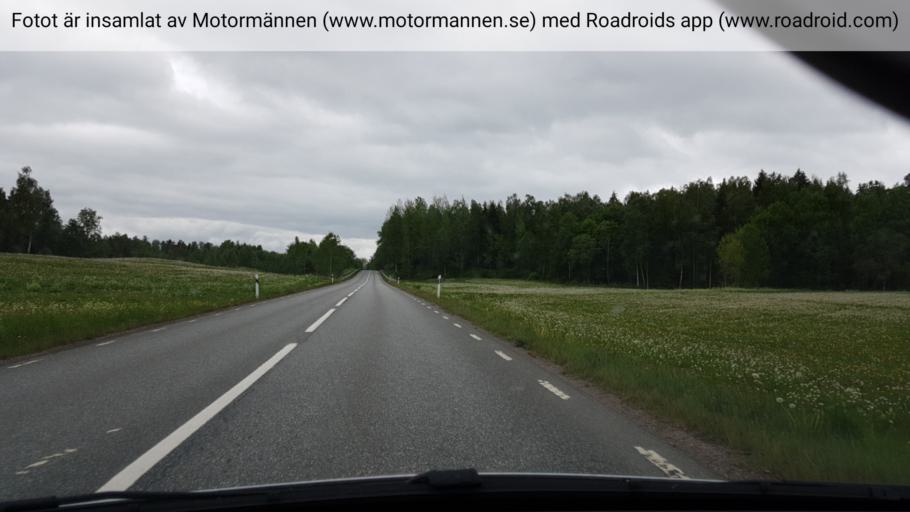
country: SE
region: Joenkoeping
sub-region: Aneby Kommun
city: Aneby
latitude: 57.9784
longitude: 14.8168
